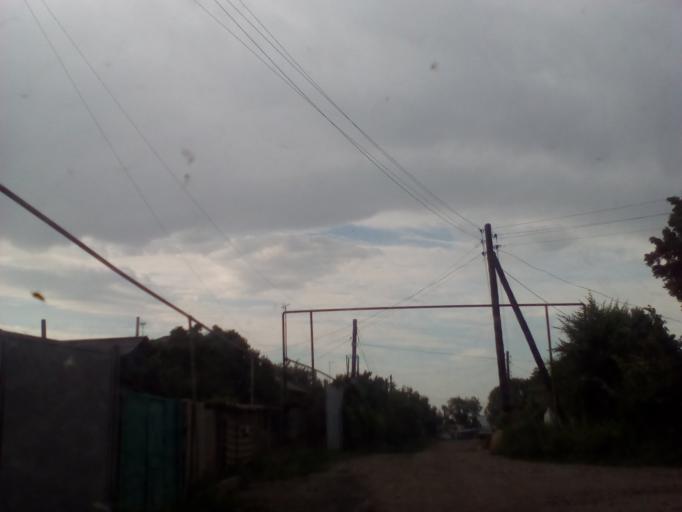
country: KZ
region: Almaty Oblysy
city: Burunday
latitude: 43.1571
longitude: 76.4057
